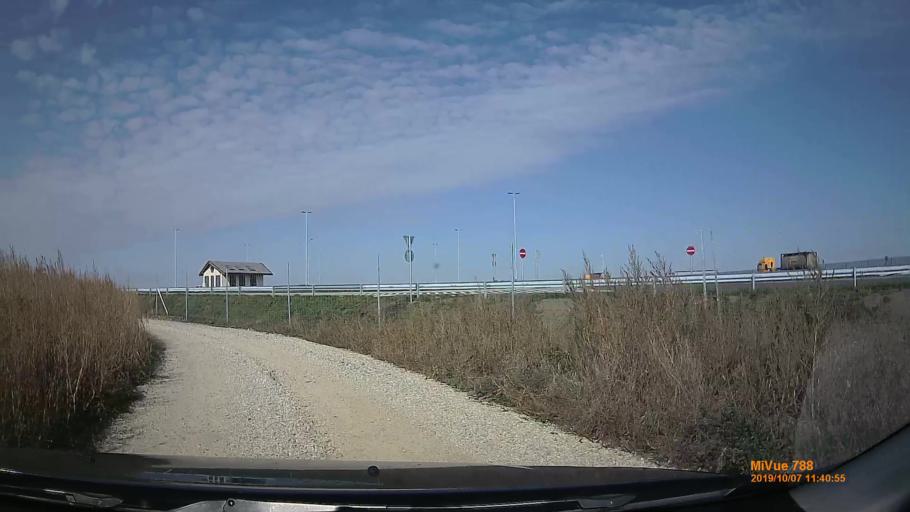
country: HU
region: Bekes
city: Kondoros
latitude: 46.7911
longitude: 20.7066
